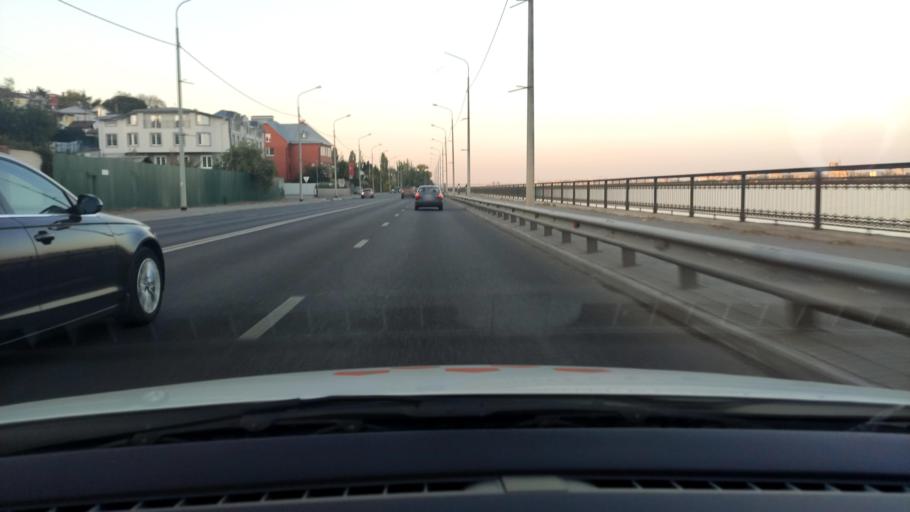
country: RU
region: Voronezj
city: Voronezh
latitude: 51.6745
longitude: 39.2256
